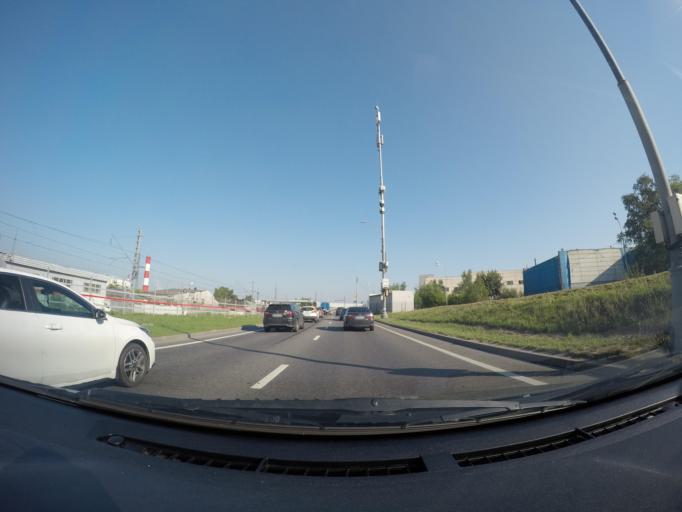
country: RU
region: Moscow
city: Ryazanskiy
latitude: 55.7481
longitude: 37.7493
